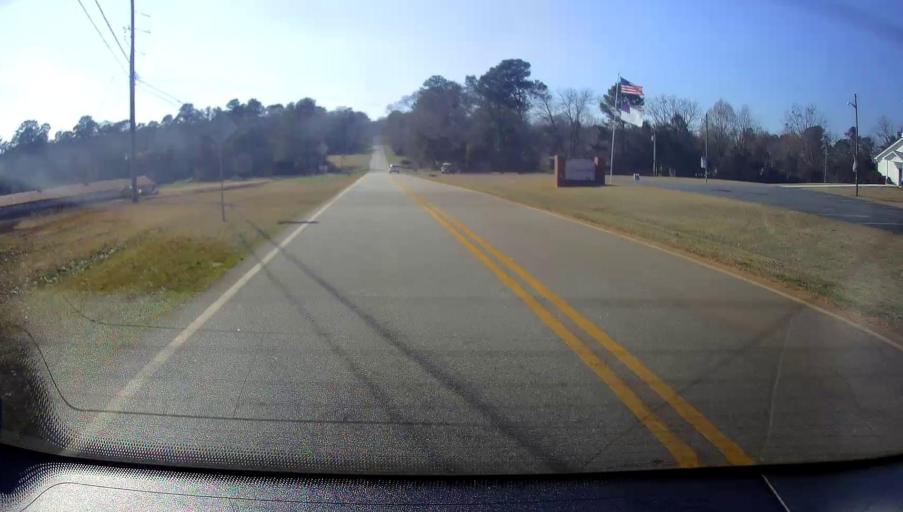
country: US
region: Georgia
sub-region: Monroe County
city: Forsyth
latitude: 33.0450
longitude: -83.9041
